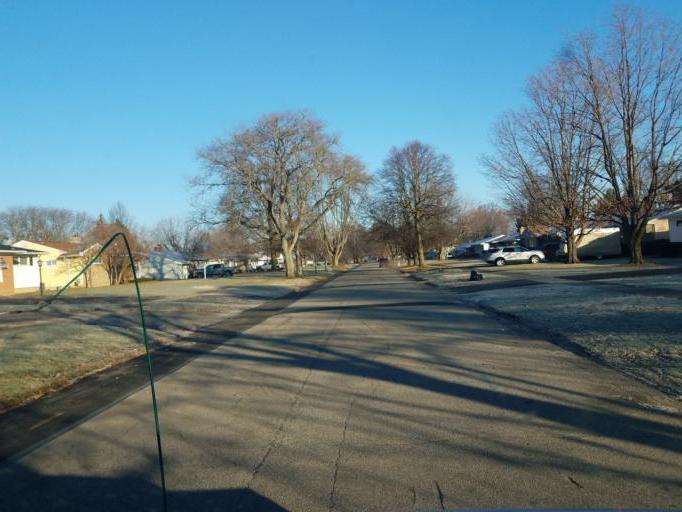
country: US
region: Ohio
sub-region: Marion County
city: Marion
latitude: 40.5820
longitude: -83.1093
